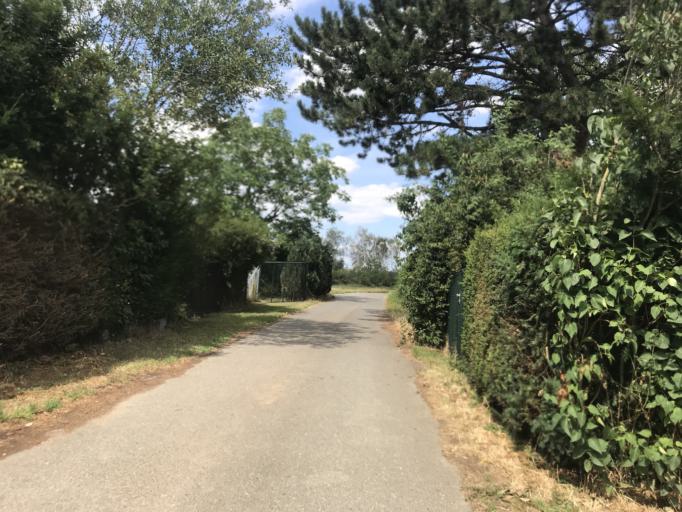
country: DE
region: Hesse
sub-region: Regierungsbezirk Darmstadt
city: Hochheim am Main
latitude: 50.0169
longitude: 8.3164
